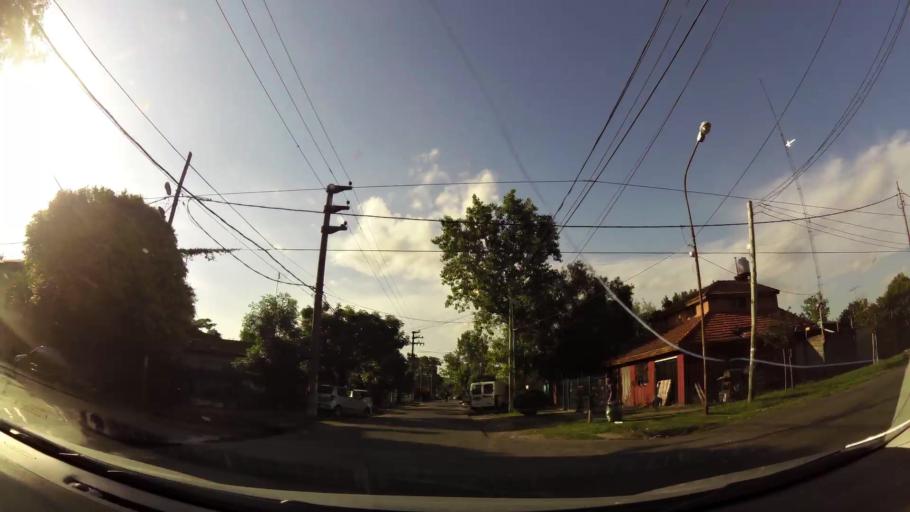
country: AR
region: Buenos Aires
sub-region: Partido de Tigre
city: Tigre
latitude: -34.4630
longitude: -58.6605
